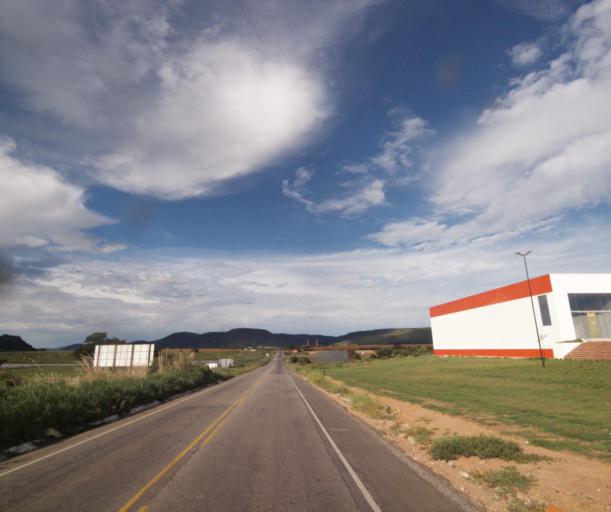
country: BR
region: Bahia
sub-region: Guanambi
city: Guanambi
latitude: -14.1885
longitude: -42.7413
